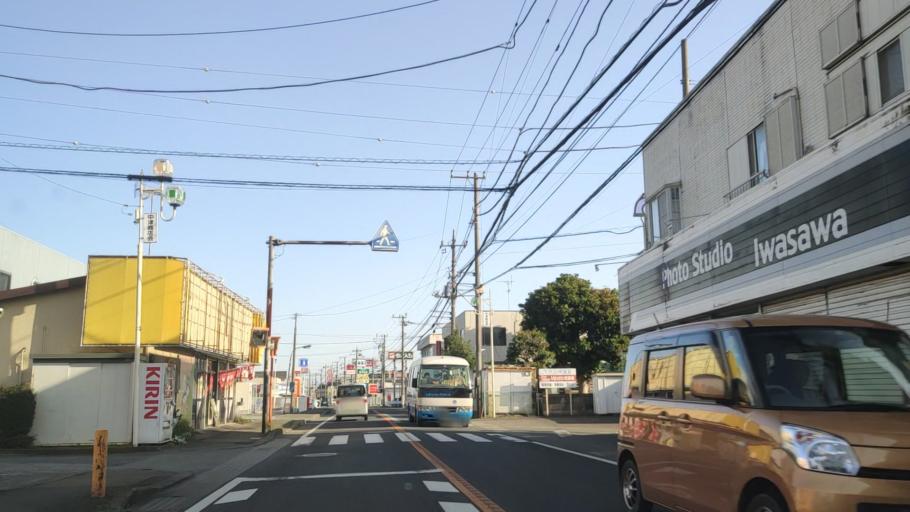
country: JP
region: Kanagawa
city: Zama
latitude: 35.5163
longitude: 139.3342
